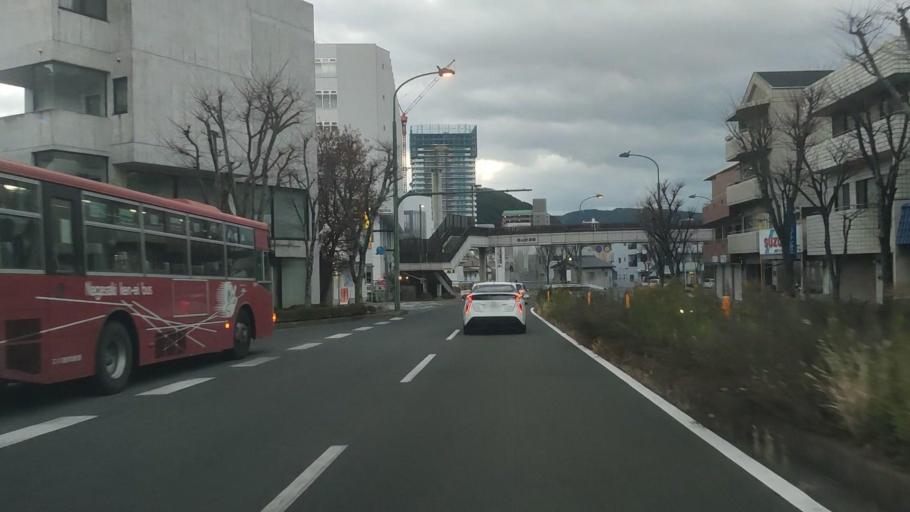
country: JP
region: Nagasaki
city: Nagasaki-shi
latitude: 32.7574
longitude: 129.8866
